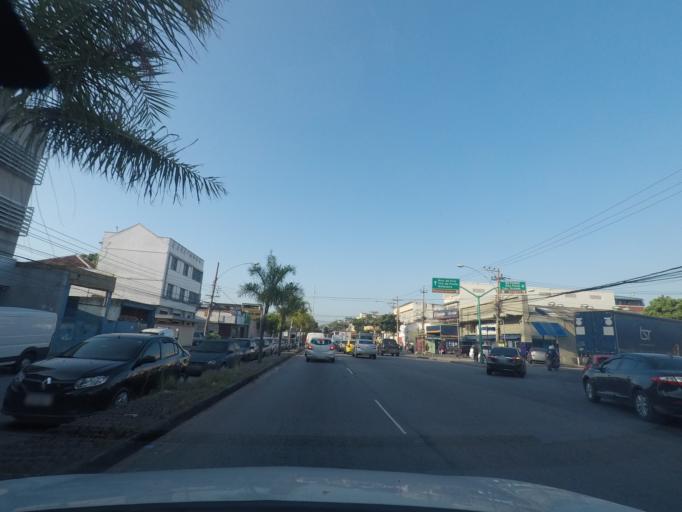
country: BR
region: Rio de Janeiro
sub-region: Duque De Caxias
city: Duque de Caxias
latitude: -22.8284
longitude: -43.2762
